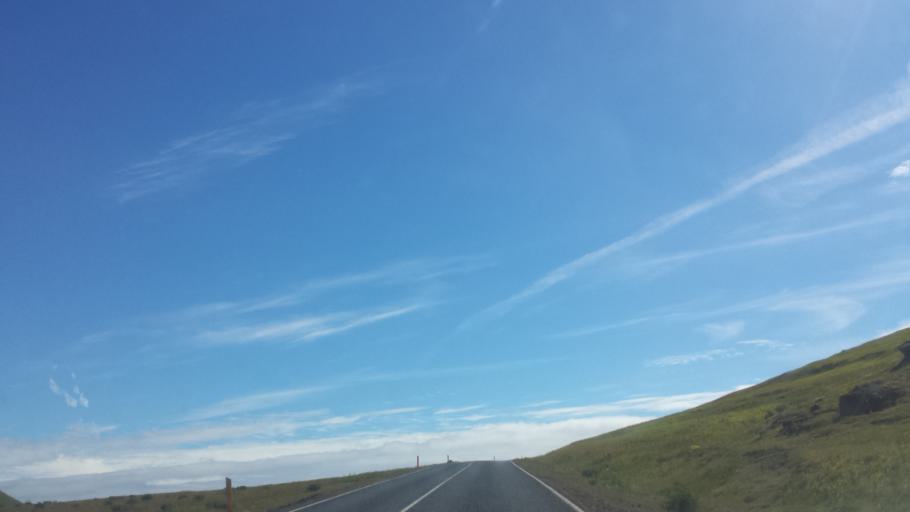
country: IS
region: South
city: Vestmannaeyjar
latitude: 63.4317
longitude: -20.2575
